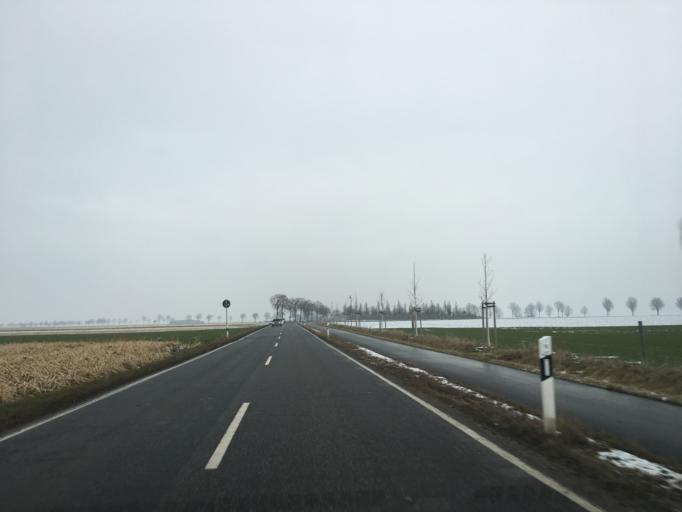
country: DE
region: North Rhine-Westphalia
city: Huckelhoven
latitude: 51.0885
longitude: 6.2455
